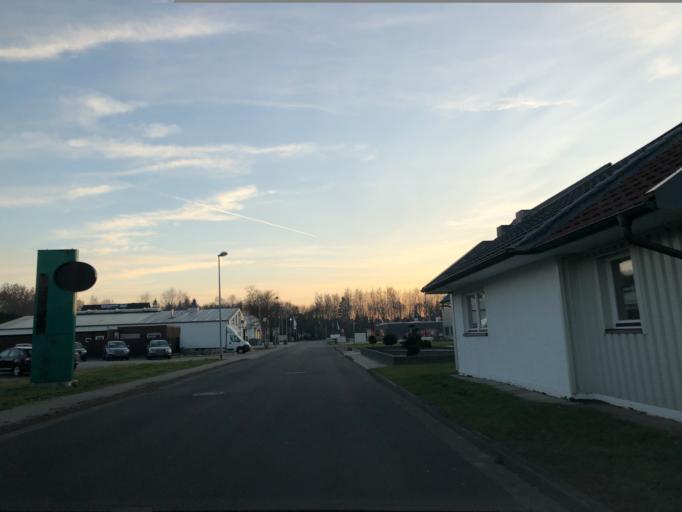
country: DE
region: Lower Saxony
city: Papenburg
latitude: 53.0929
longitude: 7.4042
